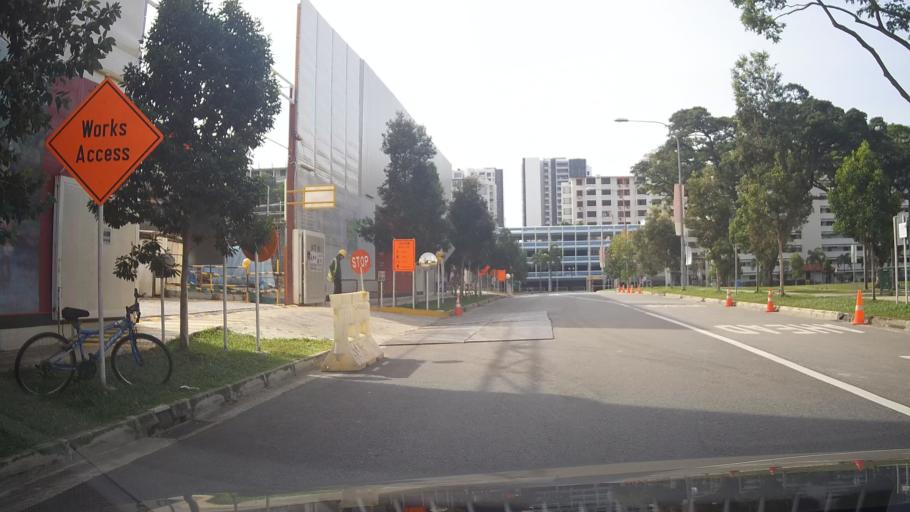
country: SG
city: Singapore
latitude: 1.3103
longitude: 103.8873
